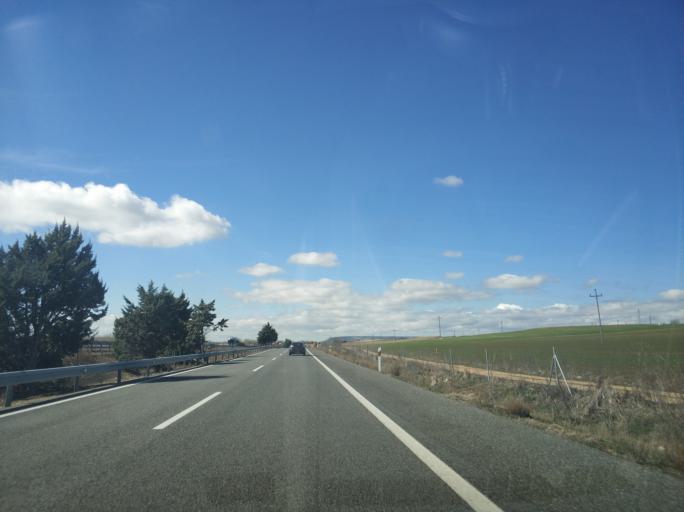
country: ES
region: Castille and Leon
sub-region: Provincia de Burgos
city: Villazopeque
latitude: 42.1866
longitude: -4.0392
